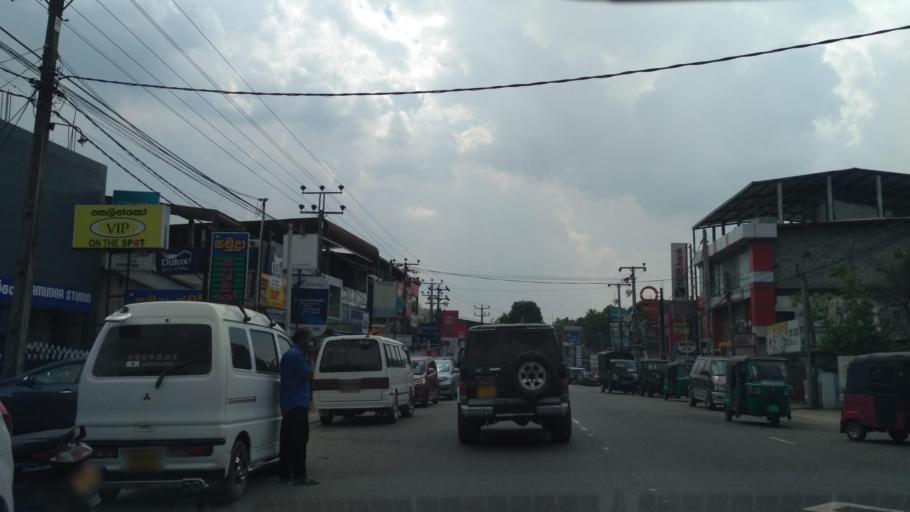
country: LK
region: North Western
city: Kuliyapitiya
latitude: 7.3286
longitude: 80.1214
